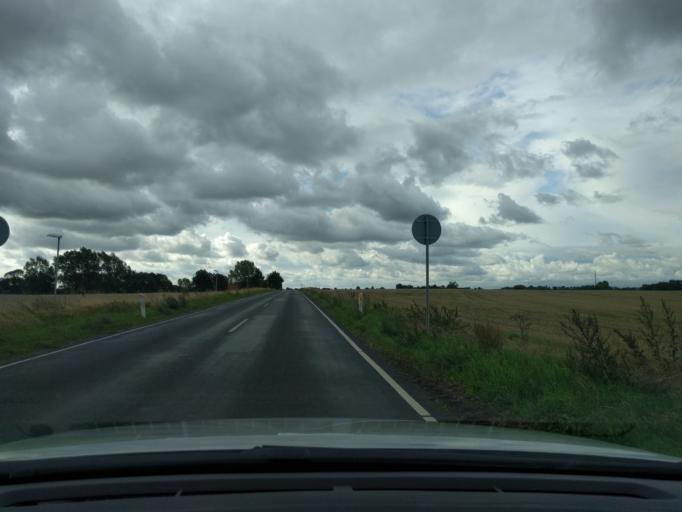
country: DK
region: South Denmark
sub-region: Nyborg Kommune
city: Ullerslev
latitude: 55.3775
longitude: 10.6663
